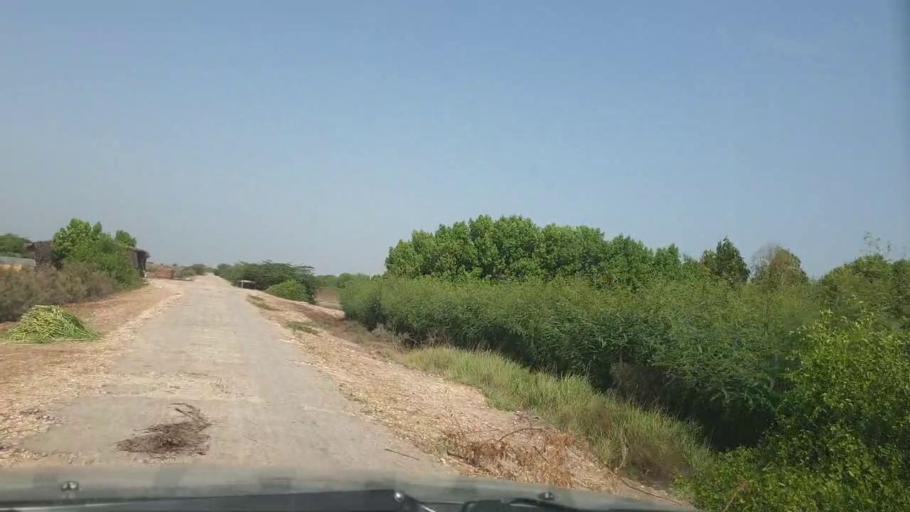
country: PK
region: Sindh
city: Tando Ghulam Ali
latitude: 25.0988
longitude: 68.8021
